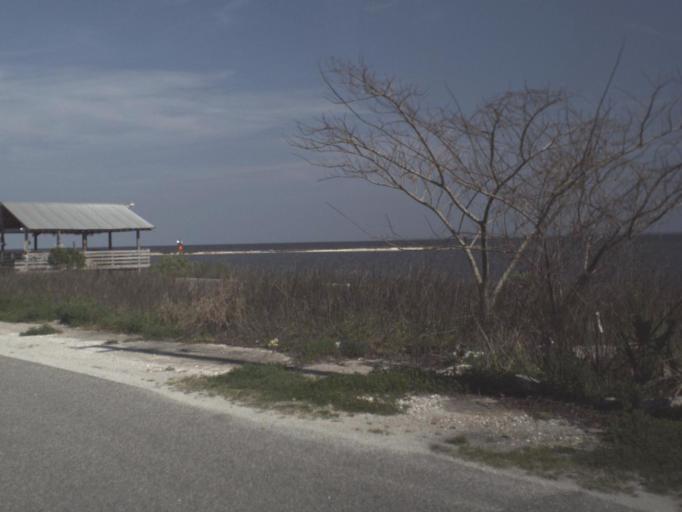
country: US
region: Florida
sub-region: Franklin County
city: Eastpoint
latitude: 29.7380
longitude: -84.8757
